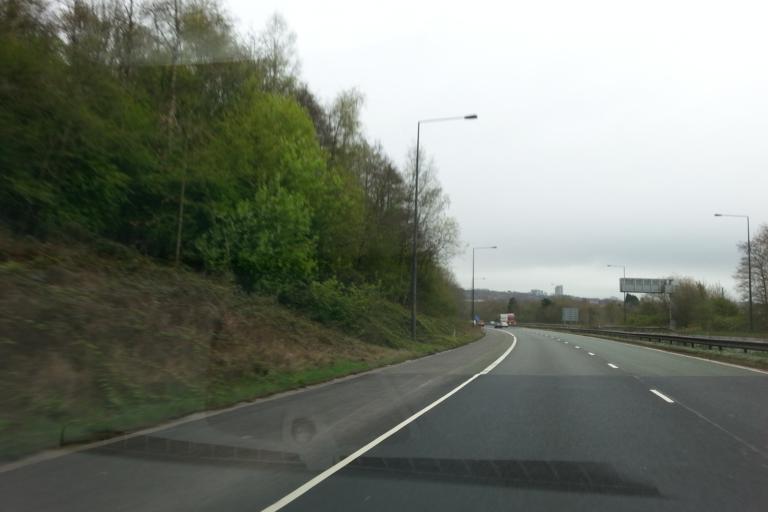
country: GB
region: England
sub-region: Borough of Oldham
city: Royton
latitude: 53.5628
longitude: -2.1533
